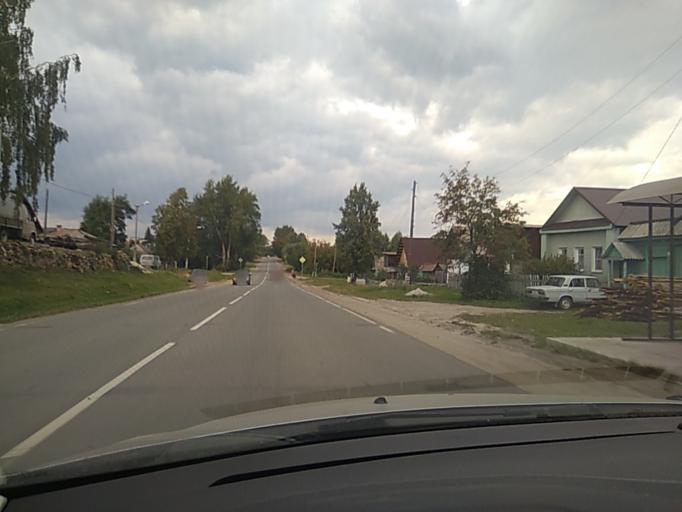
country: RU
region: Chelyabinsk
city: Kyshtym
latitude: 55.7055
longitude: 60.5186
